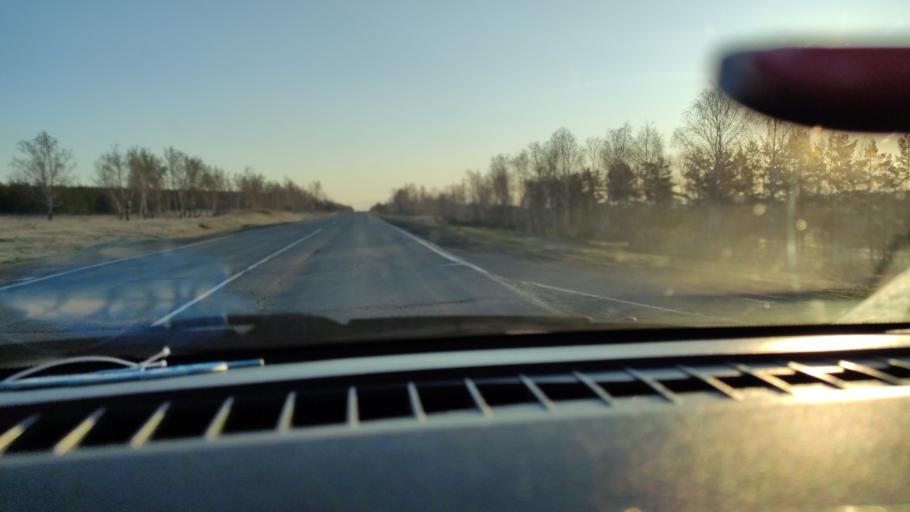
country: RU
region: Saratov
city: Sennoy
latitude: 52.1096
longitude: 46.8276
